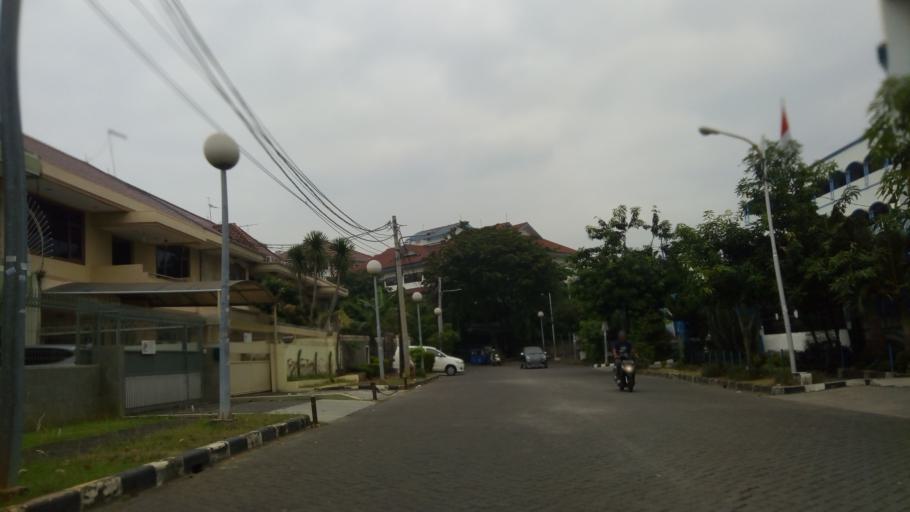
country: ID
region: Jakarta Raya
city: Jakarta
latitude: -6.1537
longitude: 106.8406
